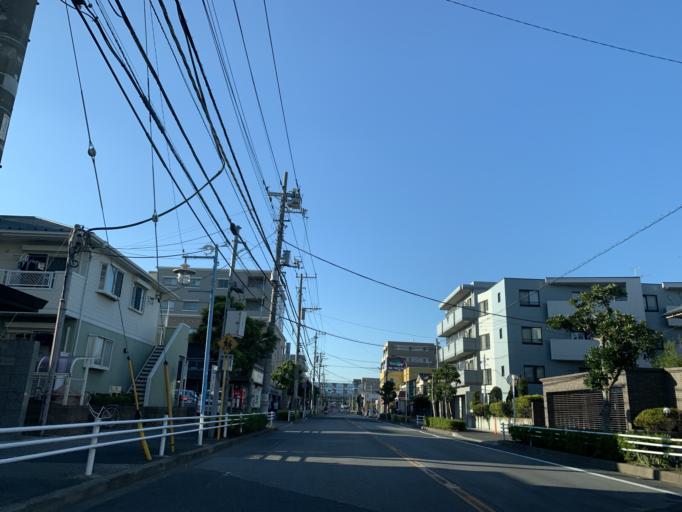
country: JP
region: Tokyo
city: Urayasu
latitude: 35.6892
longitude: 139.9265
